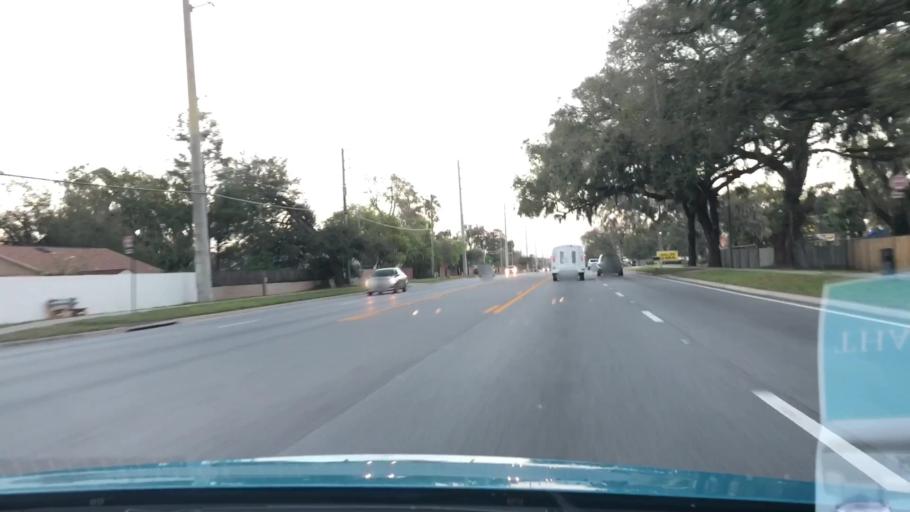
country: US
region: Florida
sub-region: Osceola County
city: Kissimmee
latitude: 28.3126
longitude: -81.3913
